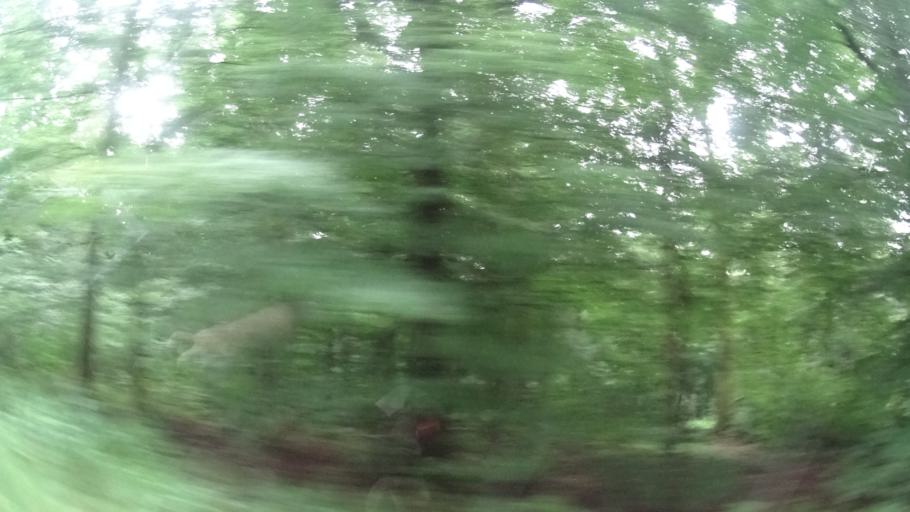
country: BE
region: Wallonia
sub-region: Province du Luxembourg
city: Saint-Leger
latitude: 49.6498
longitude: 5.6755
